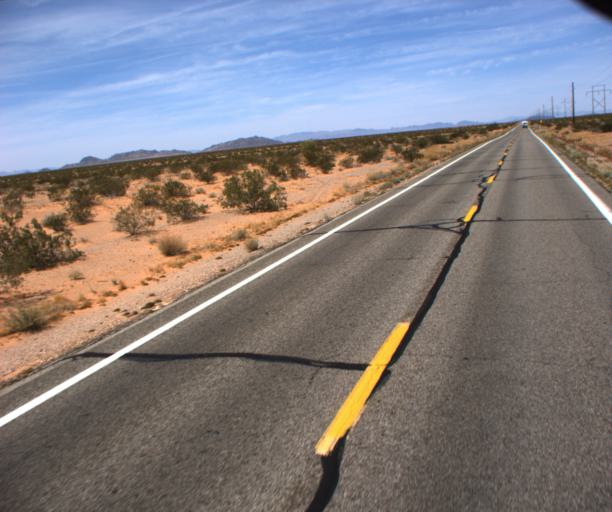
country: US
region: Arizona
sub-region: La Paz County
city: Quartzsite
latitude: 33.8669
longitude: -114.2169
